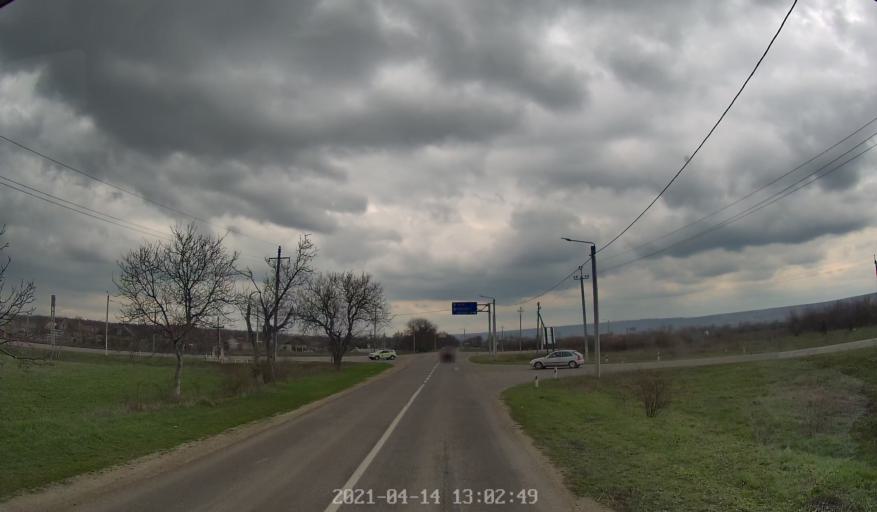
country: MD
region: Chisinau
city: Vadul lui Voda
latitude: 47.1203
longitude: 29.1111
